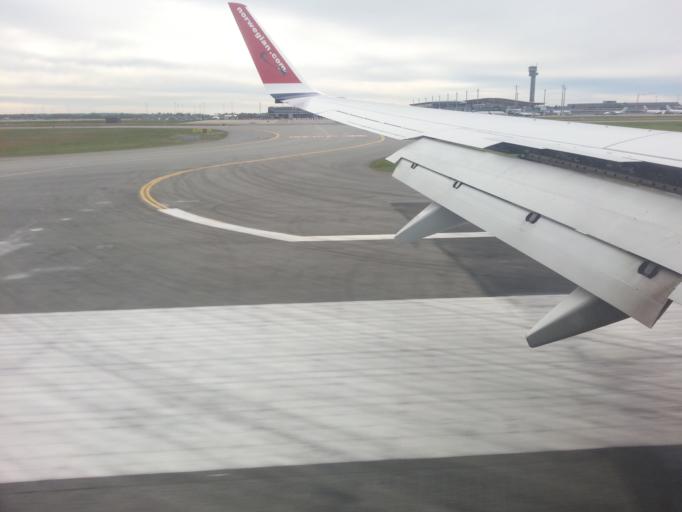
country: NO
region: Akershus
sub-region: Nannestad
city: Teigebyen
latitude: 60.1997
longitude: 11.0818
